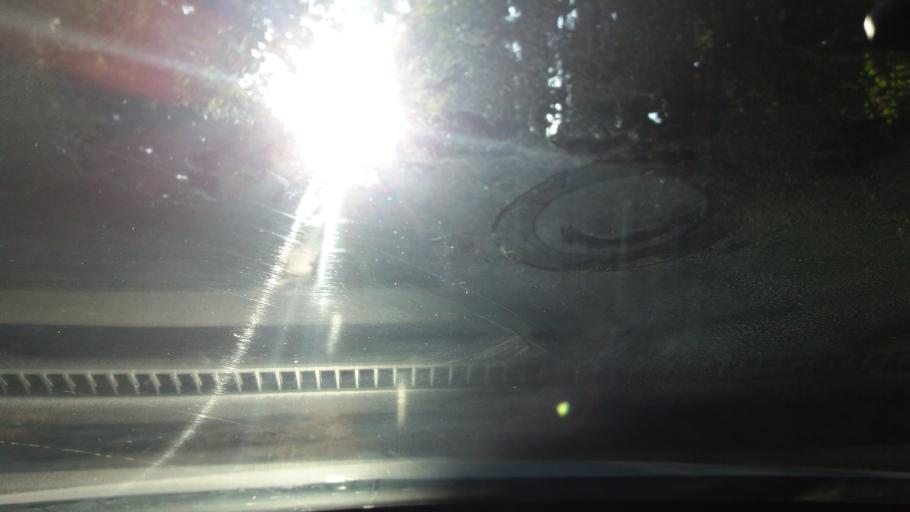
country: BR
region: Sao Paulo
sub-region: Franco Da Rocha
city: Franco da Rocha
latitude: -23.3337
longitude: -46.6867
